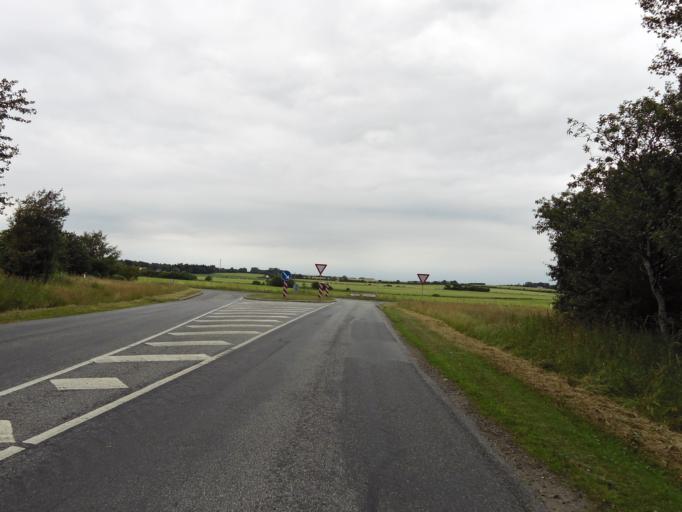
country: DK
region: South Denmark
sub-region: Tonder Kommune
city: Logumkloster
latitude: 55.1421
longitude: 8.9694
